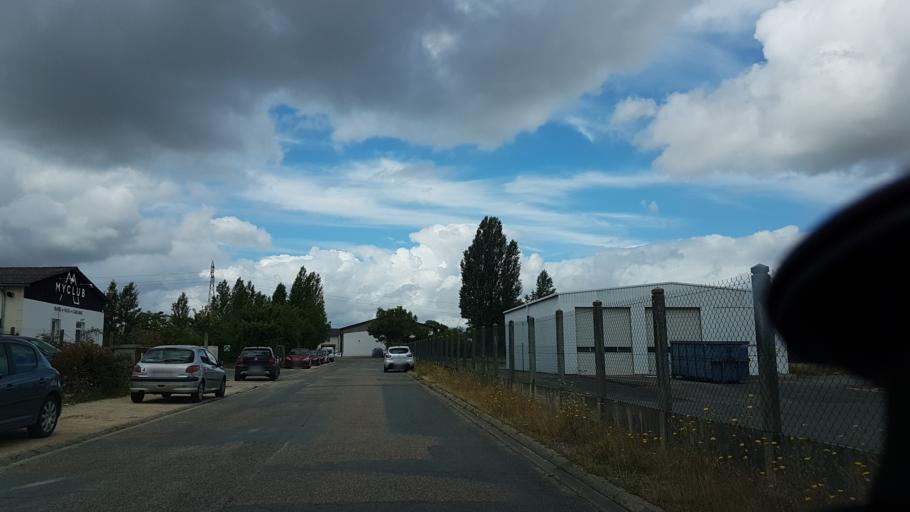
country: FR
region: Centre
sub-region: Departement du Cher
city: Bourges
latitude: 47.1054
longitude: 2.3860
